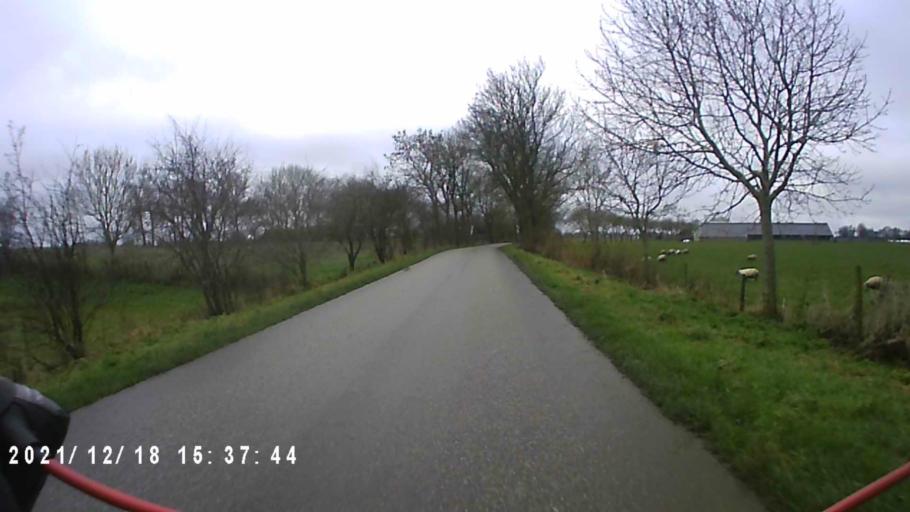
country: NL
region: Friesland
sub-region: Gemeente Dongeradeel
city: Anjum
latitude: 53.3394
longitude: 6.1227
